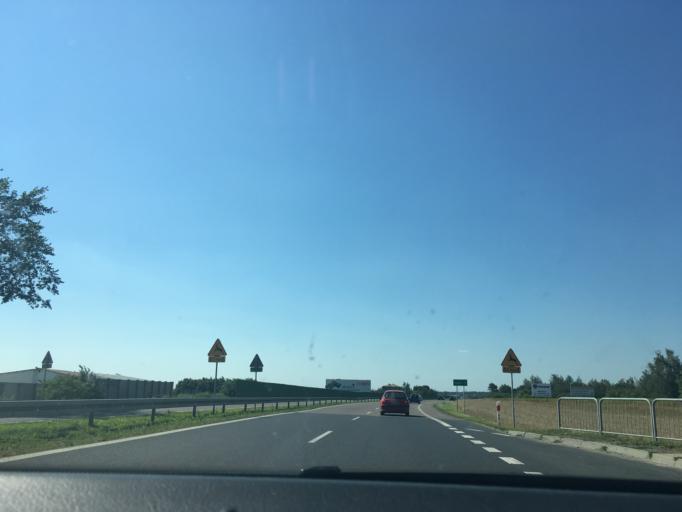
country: PL
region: Lublin Voivodeship
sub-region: Powiat lubelski
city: Niemce
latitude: 51.3373
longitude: 22.6178
